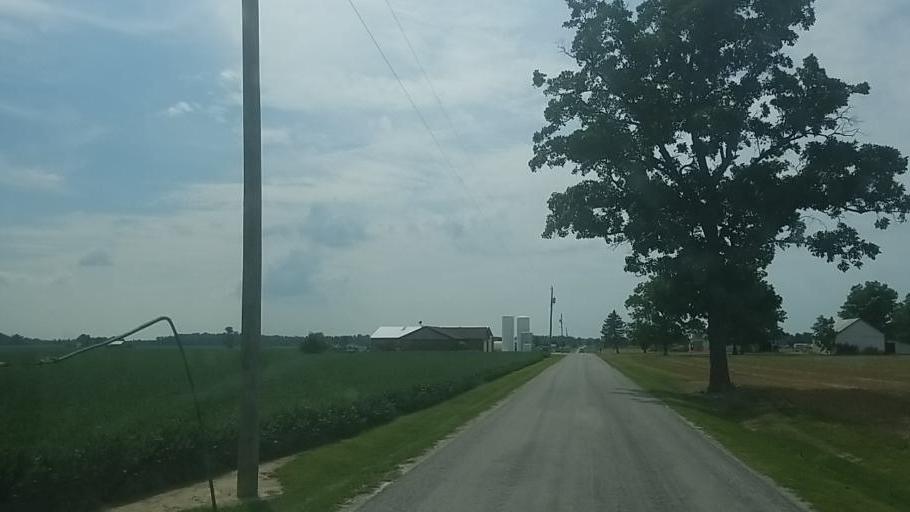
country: US
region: Ohio
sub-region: Hardin County
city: Forest
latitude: 40.7600
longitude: -83.5481
